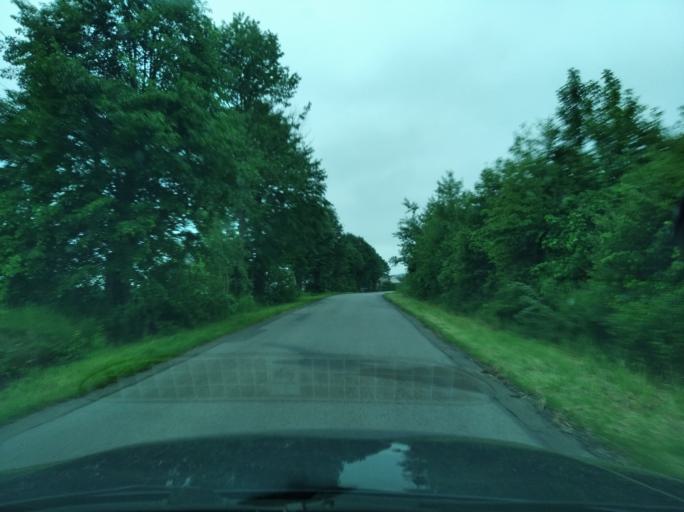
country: PL
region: Subcarpathian Voivodeship
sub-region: Powiat brzozowski
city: Orzechowka
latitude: 49.7286
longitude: 21.9401
